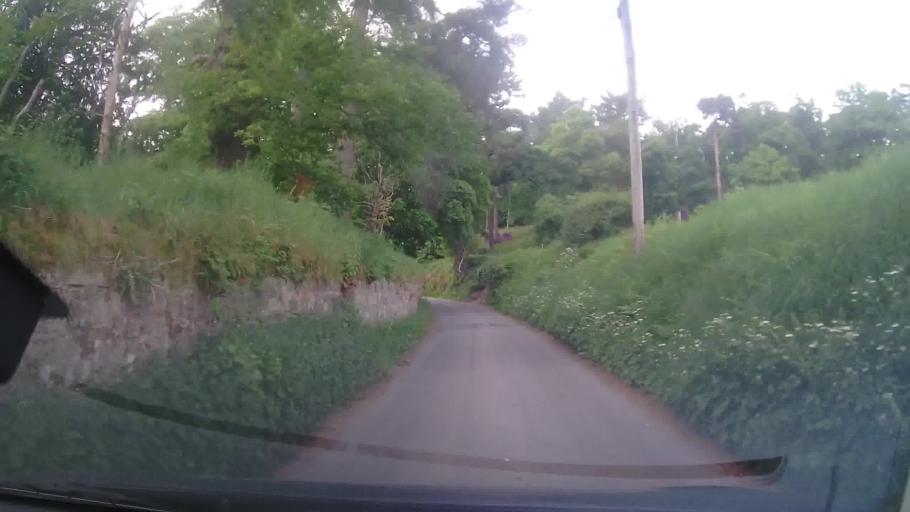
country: GB
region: England
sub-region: Shropshire
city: Clive
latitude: 52.8057
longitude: -2.7244
